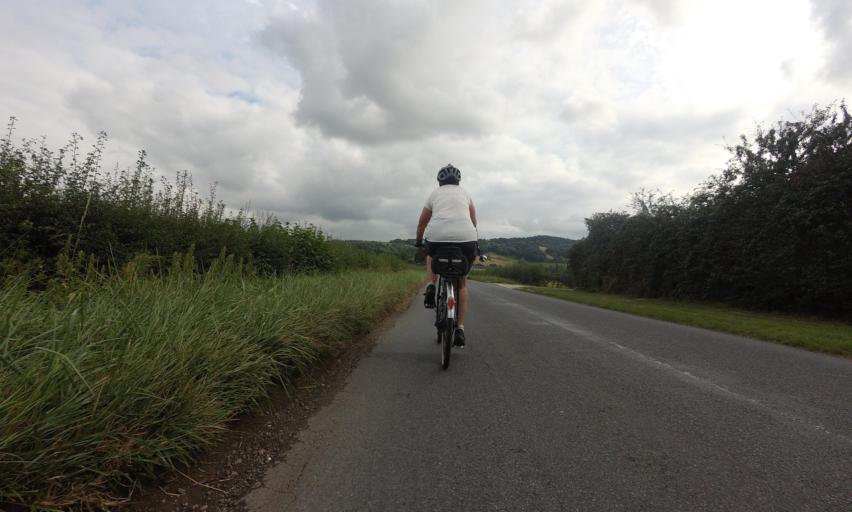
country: GB
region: England
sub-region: Gloucestershire
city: Winchcombe
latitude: 51.9779
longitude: -1.9965
